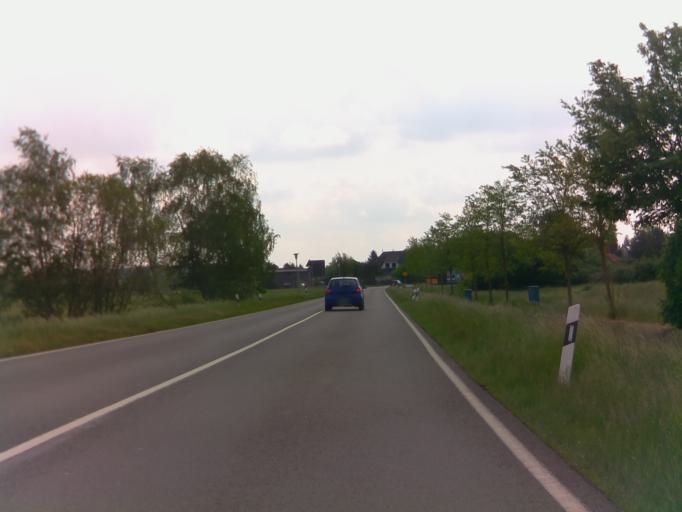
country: DE
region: Saxony-Anhalt
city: Javenitz
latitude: 52.5286
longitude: 11.4532
